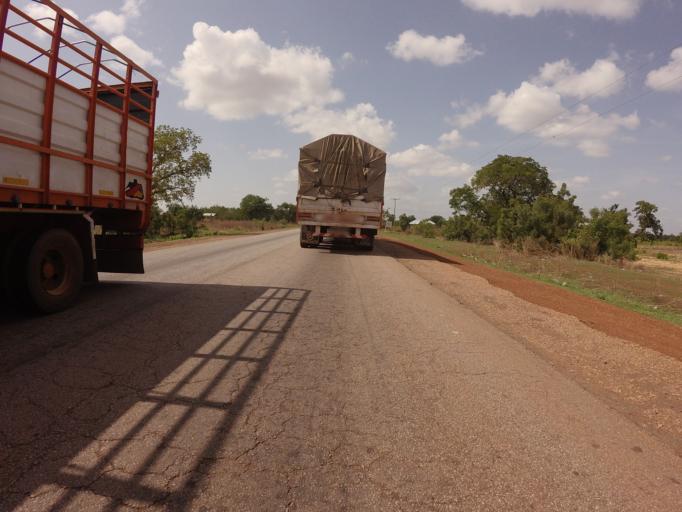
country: GH
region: Northern
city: Savelugu
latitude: 9.8774
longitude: -0.8715
